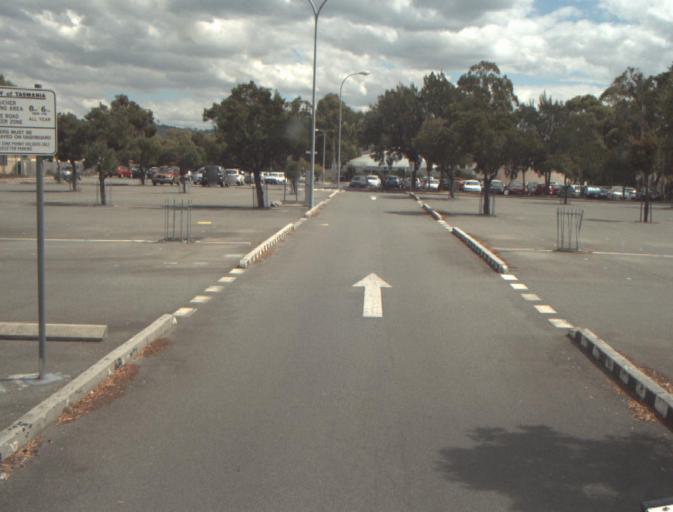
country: AU
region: Tasmania
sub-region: Launceston
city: Newnham
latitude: -41.4025
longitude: 147.1246
